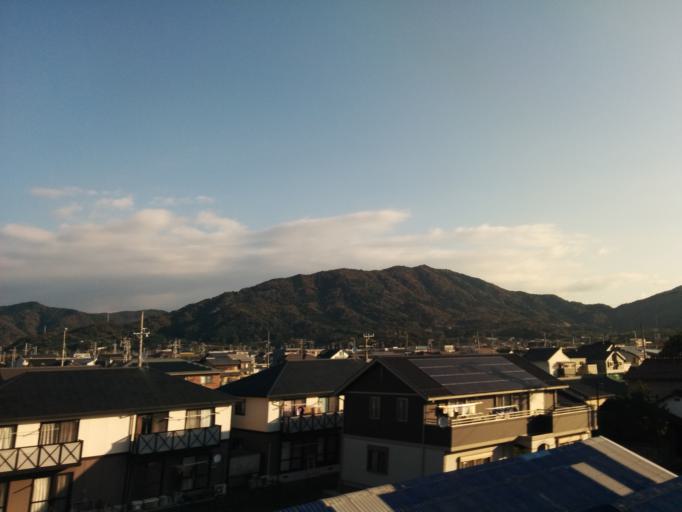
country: JP
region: Aichi
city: Gamagori
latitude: 34.8319
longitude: 137.2323
